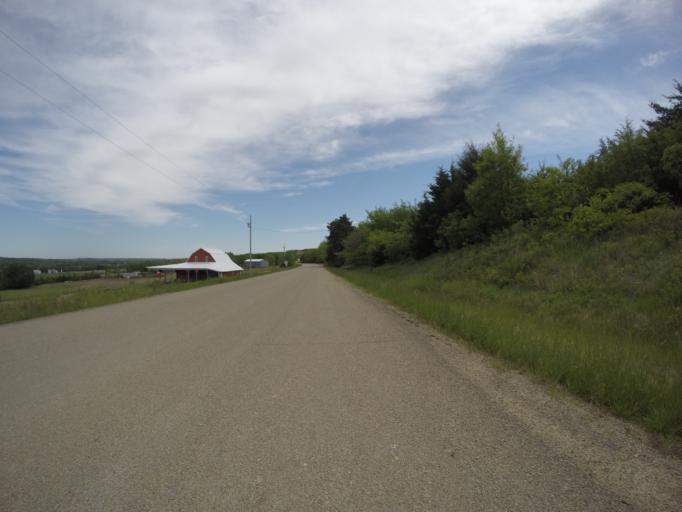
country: US
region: Kansas
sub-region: Riley County
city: Ogden
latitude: 39.0569
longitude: -96.6492
